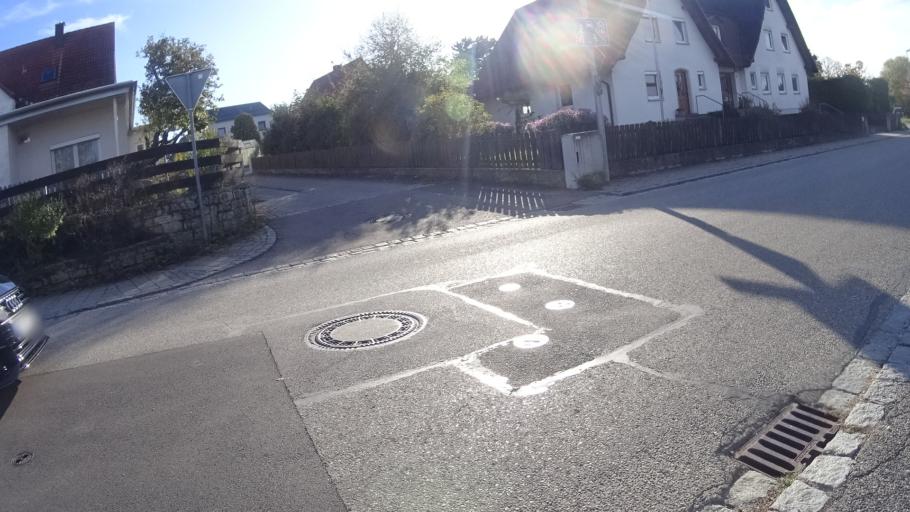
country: DE
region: Bavaria
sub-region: Upper Bavaria
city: Bohmfeld
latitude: 48.8635
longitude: 11.3623
